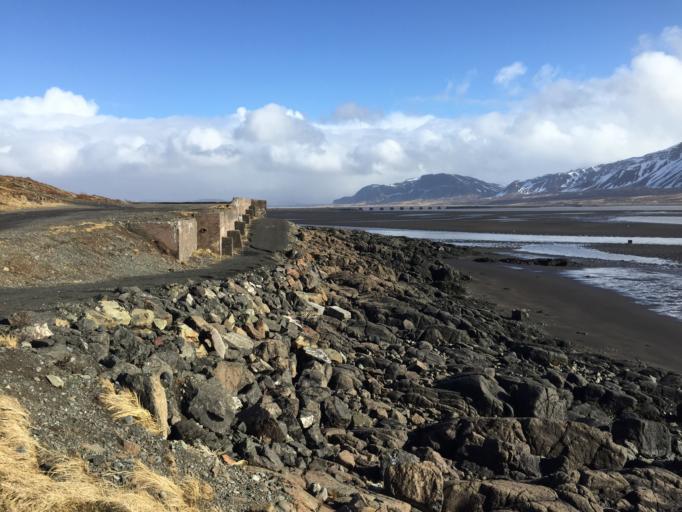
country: IS
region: West
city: Borgarnes
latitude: 64.5351
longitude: -21.9236
